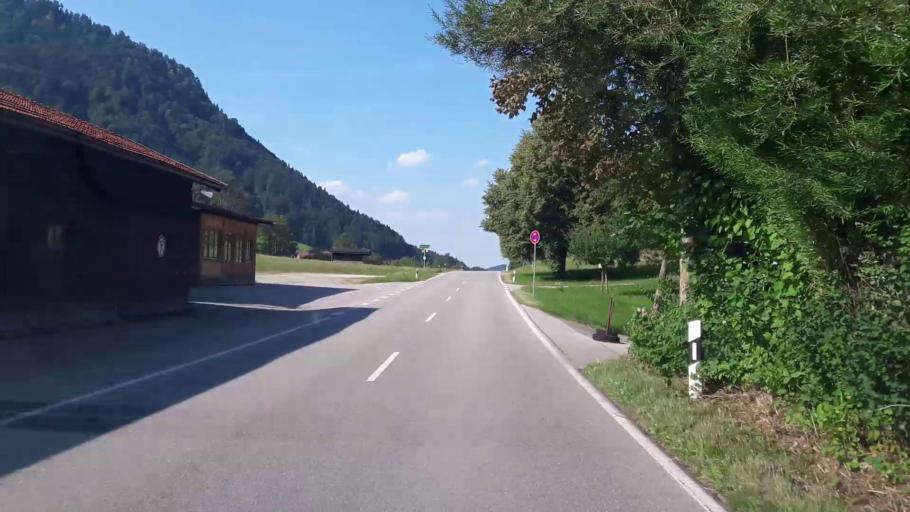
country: DE
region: Bavaria
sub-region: Upper Bavaria
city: Ruhpolding
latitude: 47.7534
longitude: 12.6303
